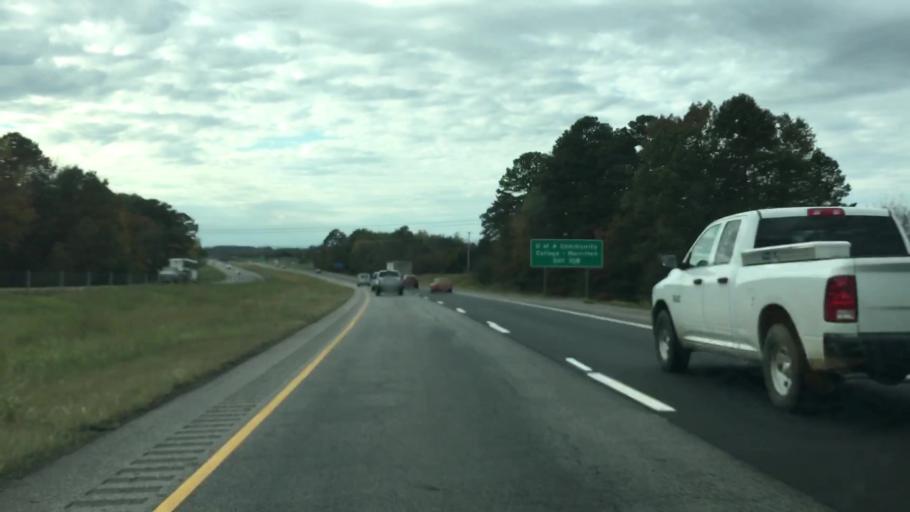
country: US
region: Arkansas
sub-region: Conway County
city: Morrilton
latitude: 35.1738
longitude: -92.7034
